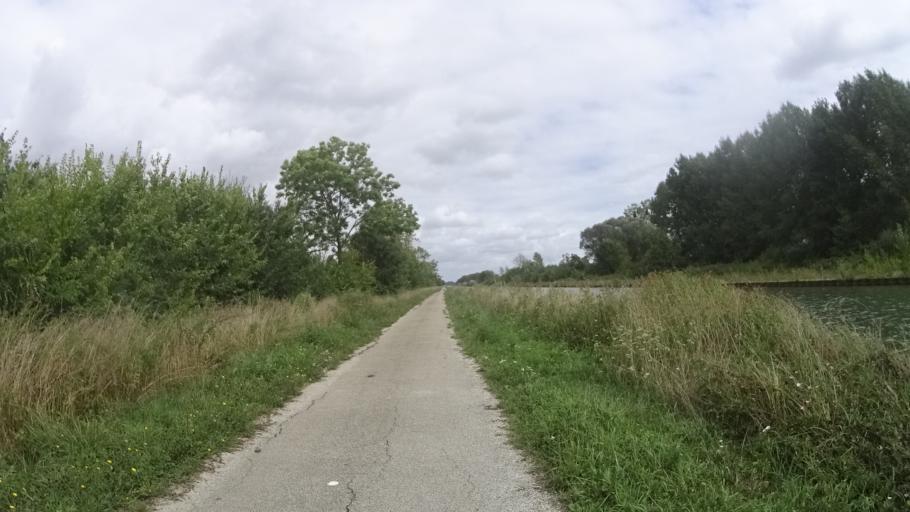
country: FR
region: Picardie
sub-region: Departement de l'Aisne
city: Ognes
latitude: 49.5945
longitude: 3.1935
